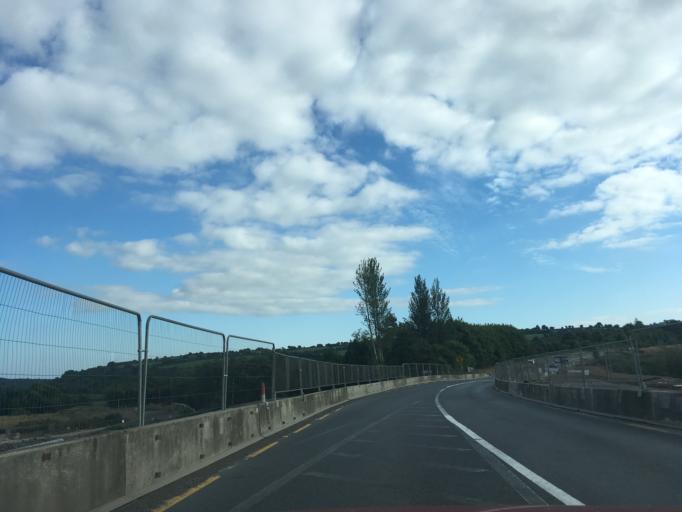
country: IE
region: Leinster
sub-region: Loch Garman
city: New Ross
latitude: 52.3603
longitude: -7.0133
